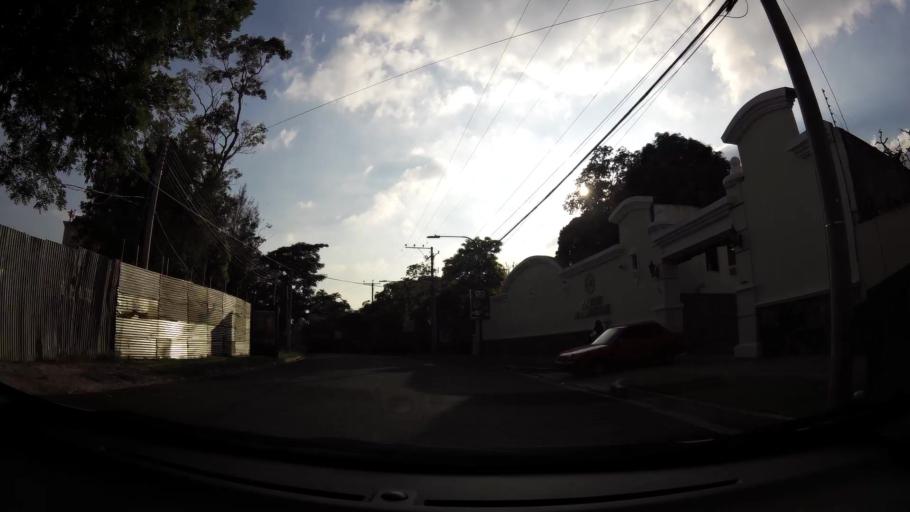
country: SV
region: La Libertad
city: Antiguo Cuscatlan
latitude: 13.6949
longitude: -89.2377
